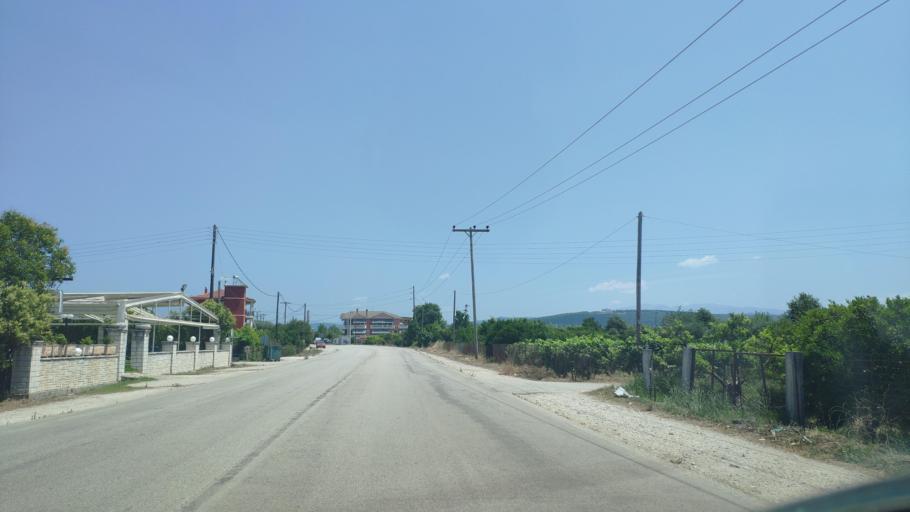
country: GR
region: Epirus
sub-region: Nomos Artas
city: Kostakioi
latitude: 39.1313
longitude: 20.9505
